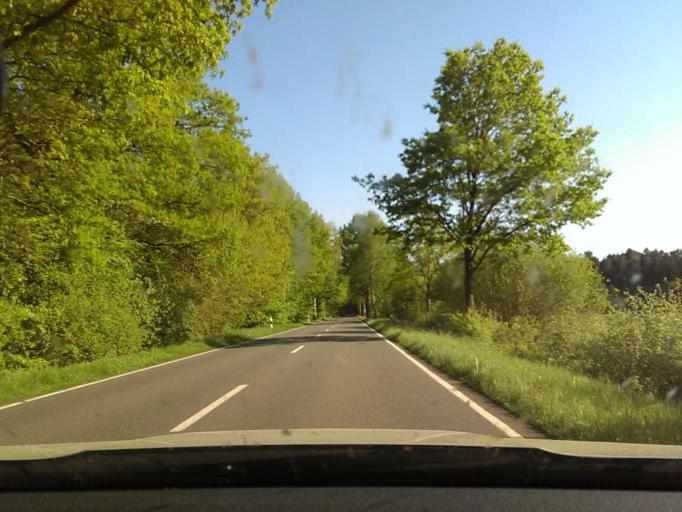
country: DE
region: Lower Saxony
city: Hambuhren
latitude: 52.5989
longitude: 9.9283
